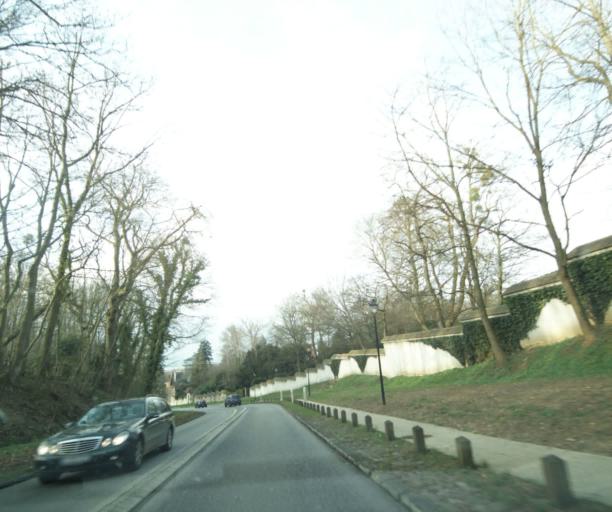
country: FR
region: Ile-de-France
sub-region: Departement des Yvelines
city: Louveciennes
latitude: 48.8613
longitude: 2.1060
